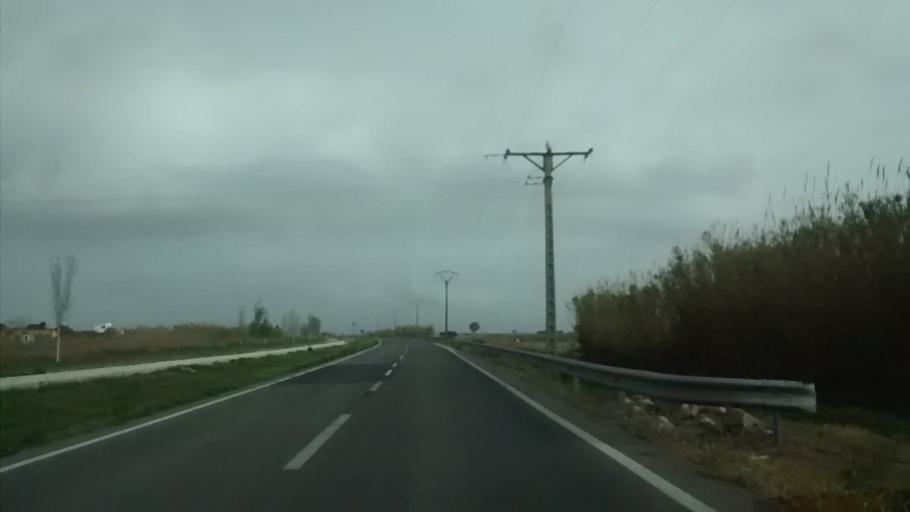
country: ES
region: Catalonia
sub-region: Provincia de Tarragona
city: Sant Carles de la Rapita
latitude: 40.6329
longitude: 0.6015
